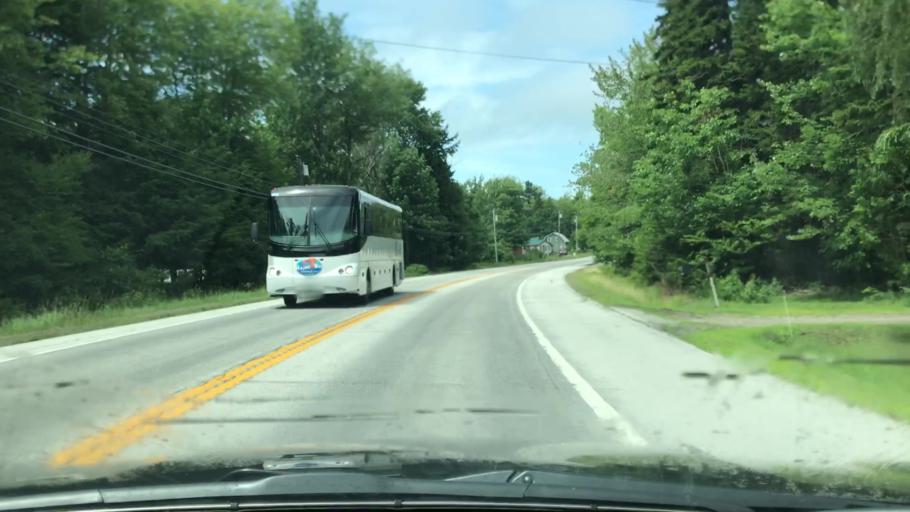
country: US
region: Maine
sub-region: Waldo County
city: Northport
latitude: 44.3442
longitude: -68.9697
